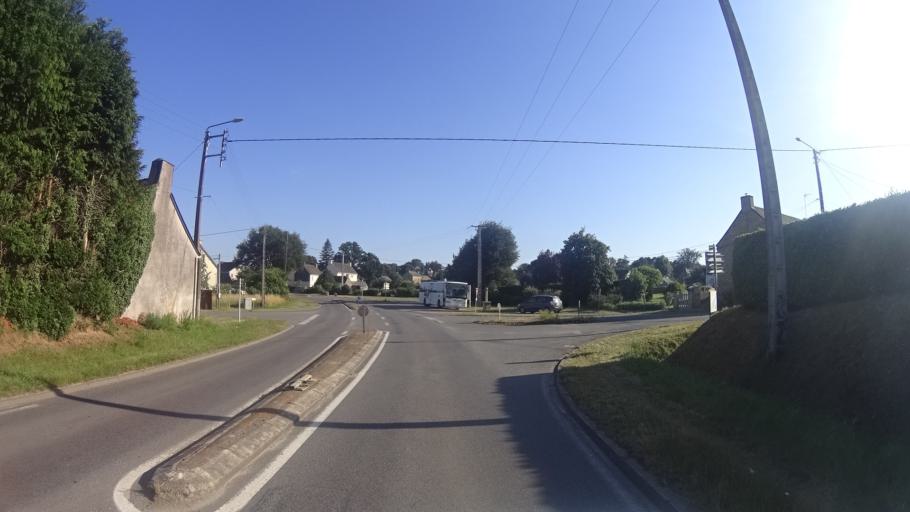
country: FR
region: Brittany
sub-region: Departement du Morbihan
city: Rieux
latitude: 47.6119
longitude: -2.1125
